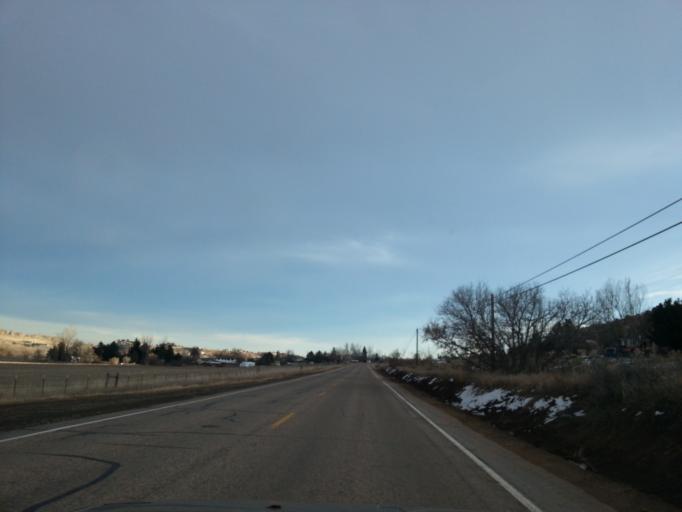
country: US
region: Colorado
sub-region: Larimer County
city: Loveland
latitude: 40.4424
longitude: -105.2005
